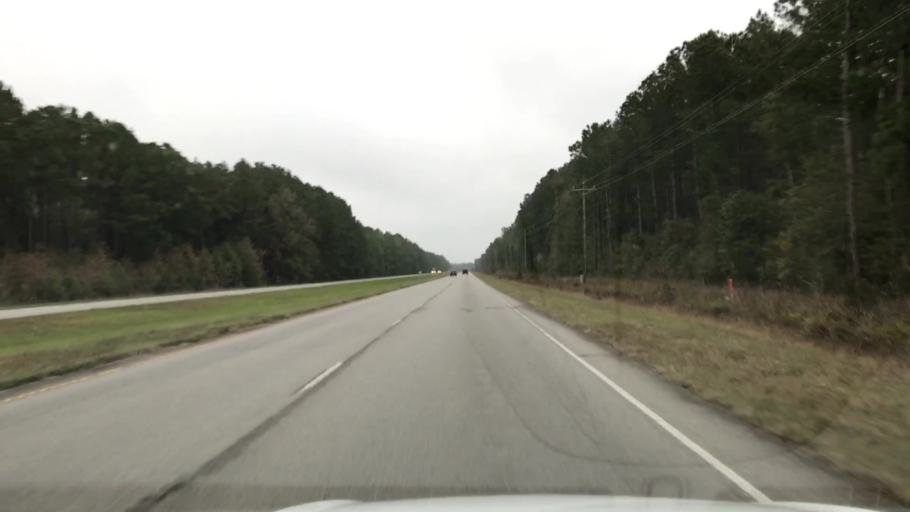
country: US
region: South Carolina
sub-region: Charleston County
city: Awendaw
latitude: 33.0125
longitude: -79.6371
